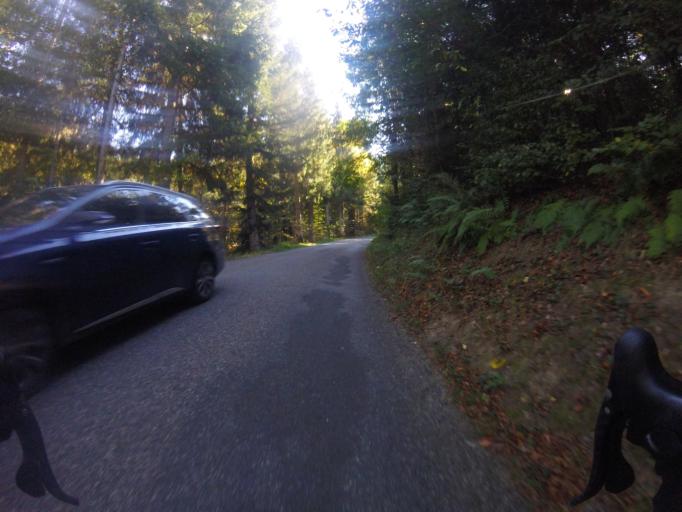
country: CH
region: Bern
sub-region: Seeland District
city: Schupfen
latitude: 47.0306
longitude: 7.3918
